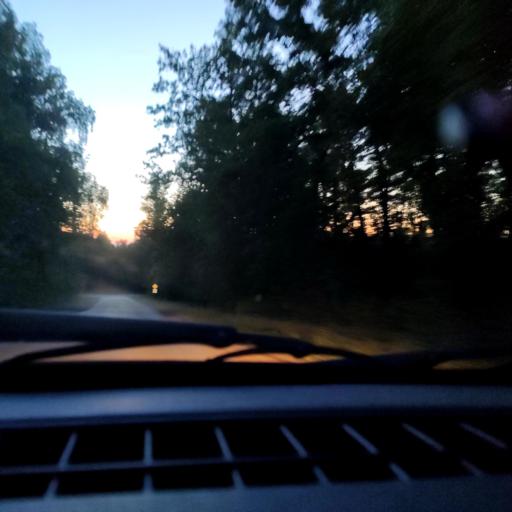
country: RU
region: Bashkortostan
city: Avdon
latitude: 54.6536
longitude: 55.5867
